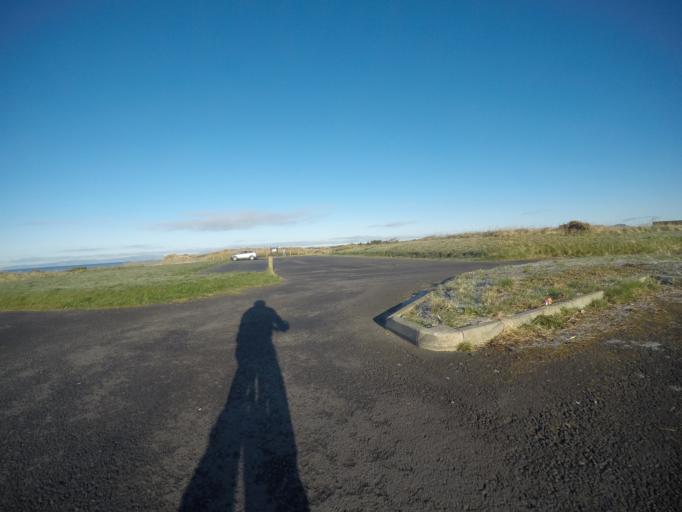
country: GB
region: Scotland
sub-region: North Ayrshire
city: Stevenston
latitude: 55.6306
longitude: -4.7543
